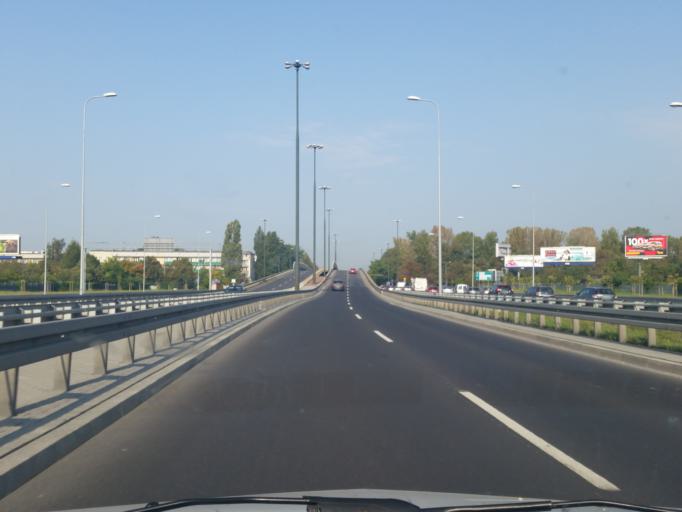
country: PL
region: Masovian Voivodeship
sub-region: Warszawa
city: Wlochy
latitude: 52.1825
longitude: 20.9825
